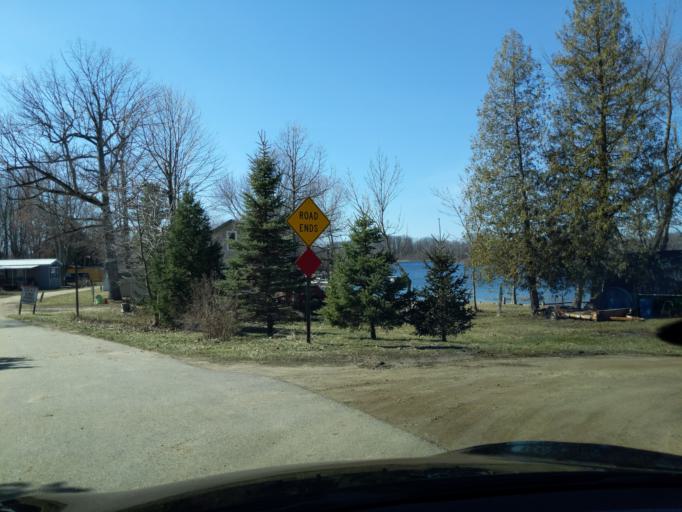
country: US
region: Michigan
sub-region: Ionia County
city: Lake Odessa
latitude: 42.7269
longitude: -85.0551
